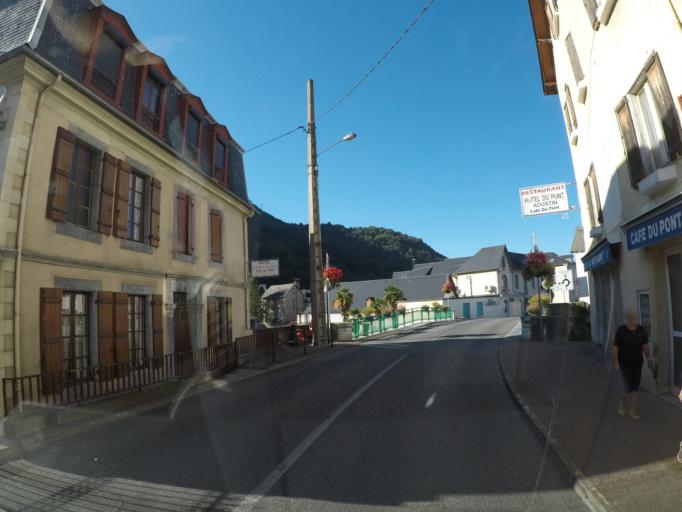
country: FR
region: Midi-Pyrenees
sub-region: Departement des Hautes-Pyrenees
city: Pierrefitte-Nestalas
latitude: 42.9569
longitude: -0.0751
